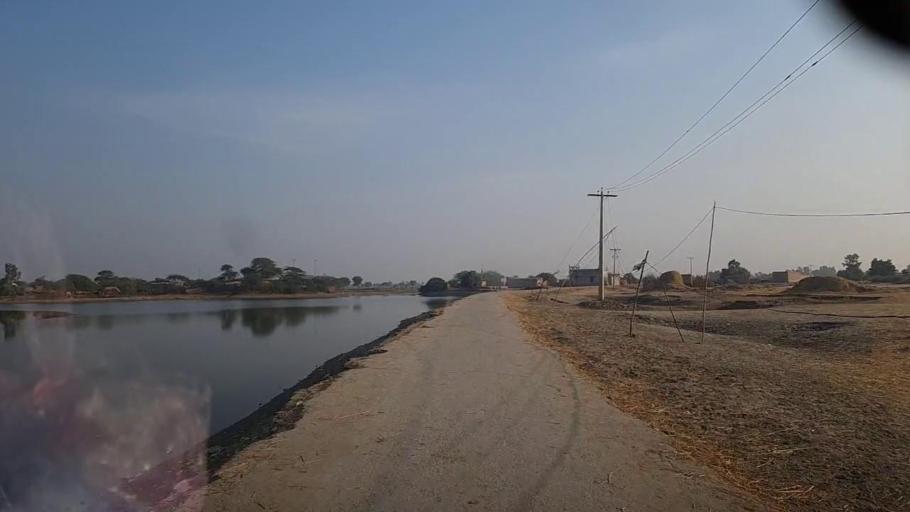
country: PK
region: Sindh
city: Jacobabad
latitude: 28.2374
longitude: 68.4834
